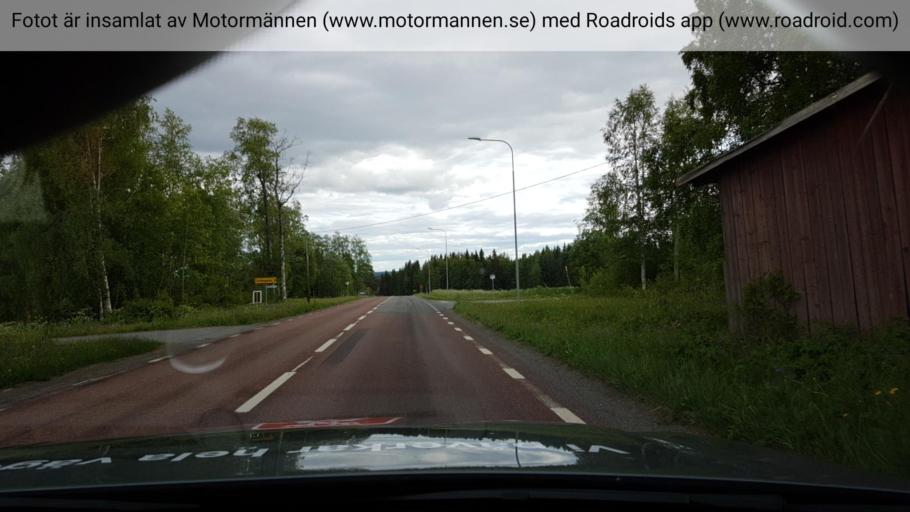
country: SE
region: Jaemtland
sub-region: Stroemsunds Kommun
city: Stroemsund
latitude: 63.8167
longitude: 15.5192
